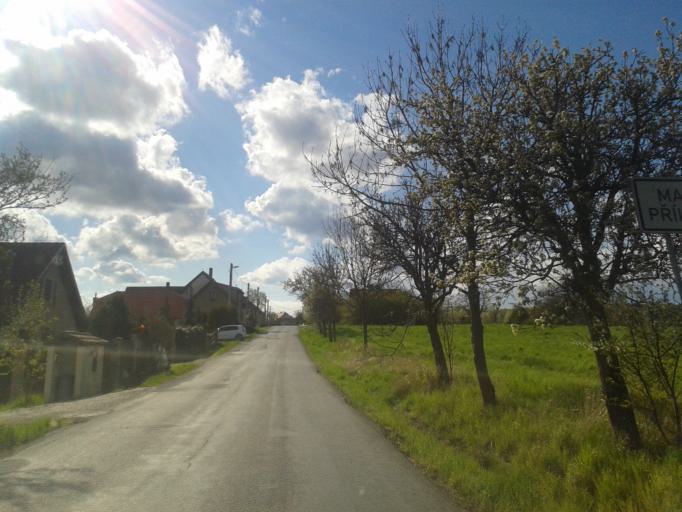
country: CZ
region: Central Bohemia
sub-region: Okres Beroun
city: Lodenice
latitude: 50.0107
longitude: 14.1211
